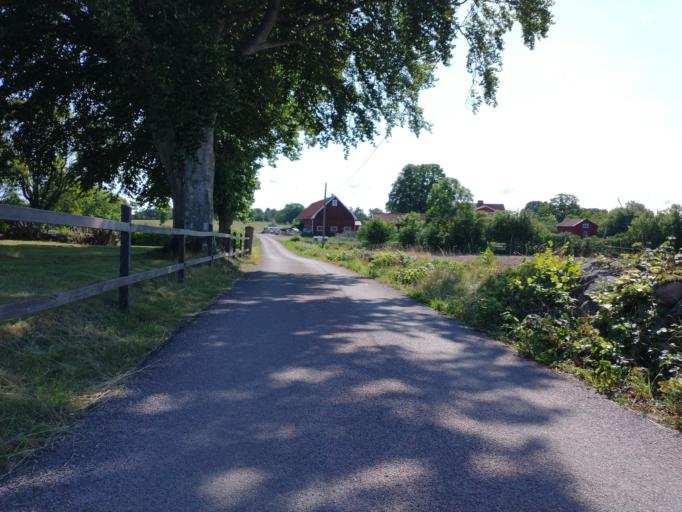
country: SE
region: Kalmar
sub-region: Kalmar Kommun
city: Lindsdal
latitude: 56.7928
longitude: 16.2892
